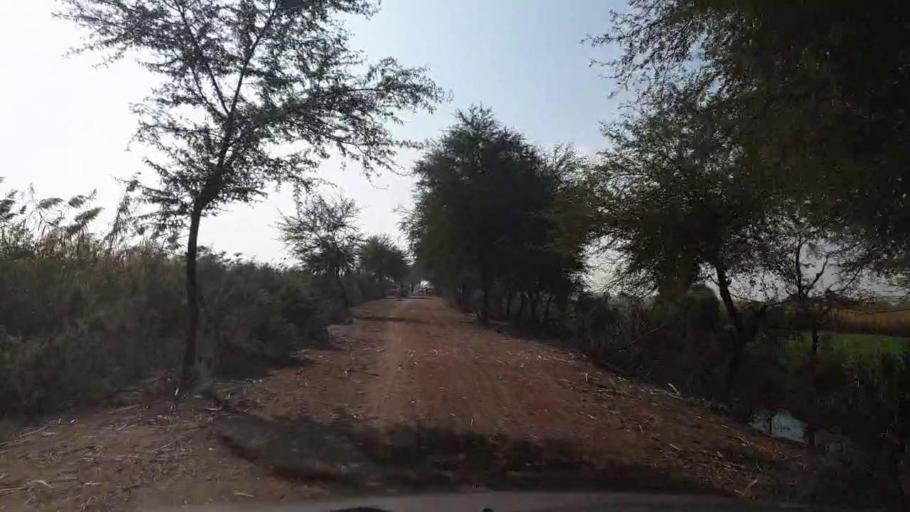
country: PK
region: Sindh
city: Sinjhoro
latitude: 26.0528
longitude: 68.7833
